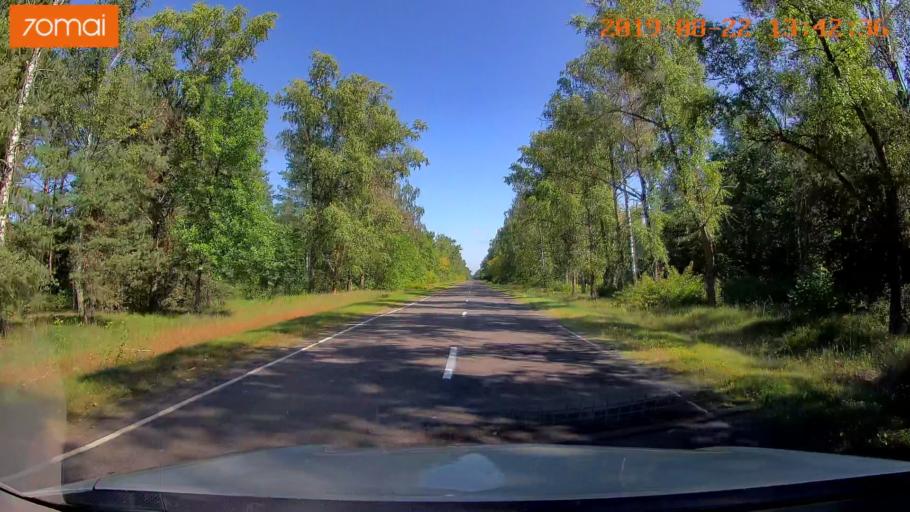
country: BY
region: Mogilev
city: Asipovichy
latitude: 53.2413
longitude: 28.4171
